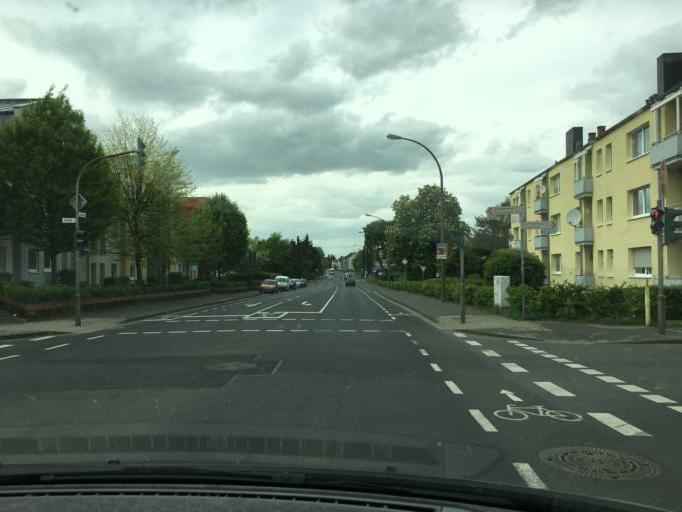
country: DE
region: North Rhine-Westphalia
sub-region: Regierungsbezirk Koln
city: Euskirchen
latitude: 50.6652
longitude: 6.7978
